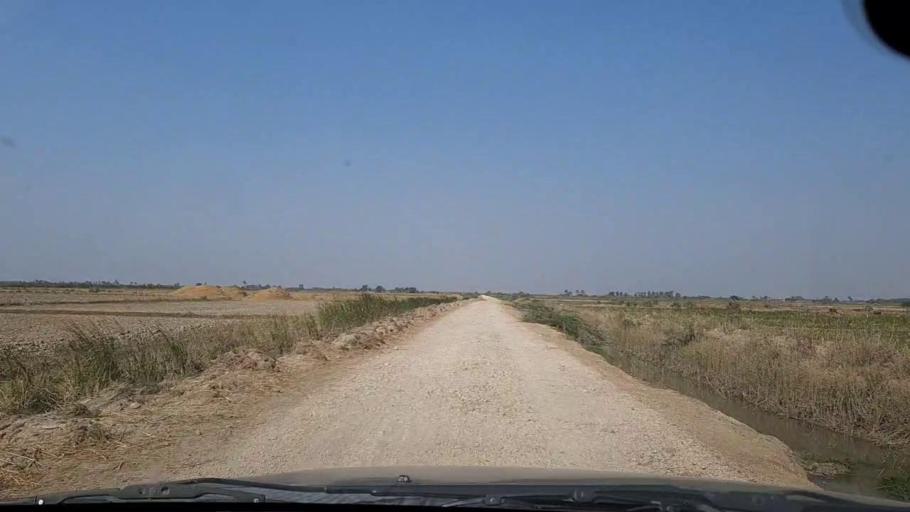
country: PK
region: Sindh
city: Mirpur Sakro
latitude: 24.3670
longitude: 67.6830
